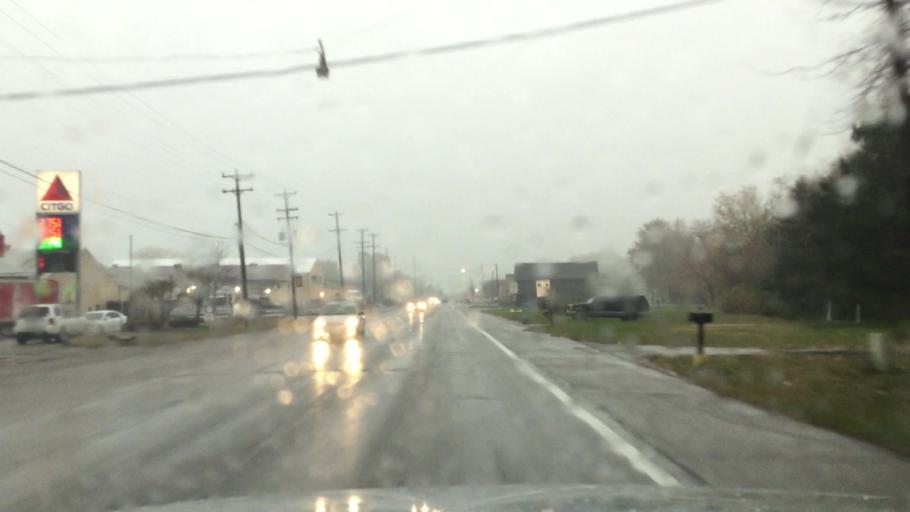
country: US
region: Michigan
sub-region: Saint Clair County
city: Pearl Beach
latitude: 42.6794
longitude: -82.6543
